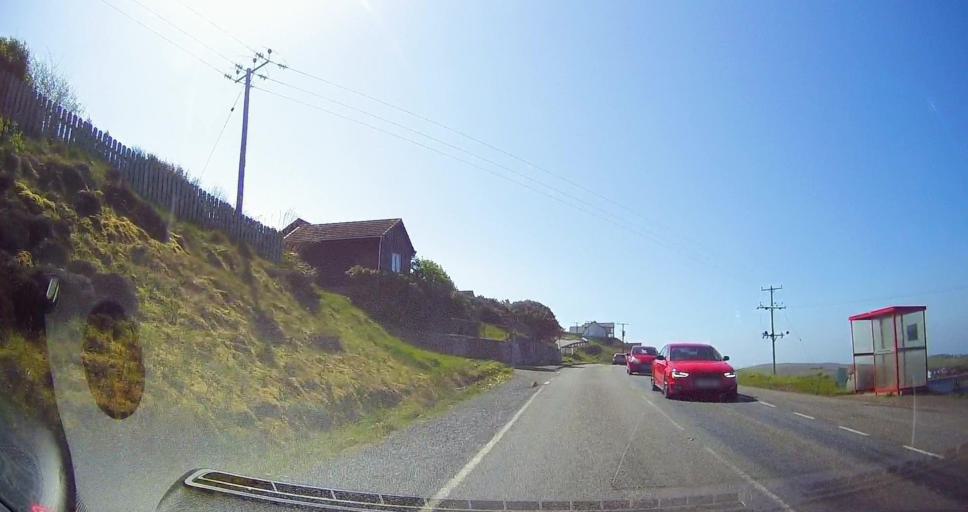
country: GB
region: Scotland
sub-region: Shetland Islands
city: Lerwick
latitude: 60.1321
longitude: -1.2673
